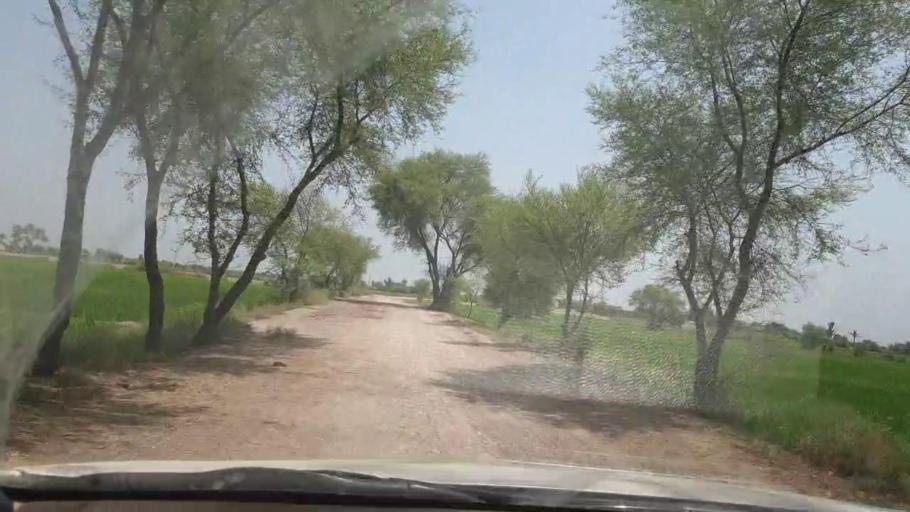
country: PK
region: Sindh
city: Lakhi
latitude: 27.8823
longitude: 68.7437
